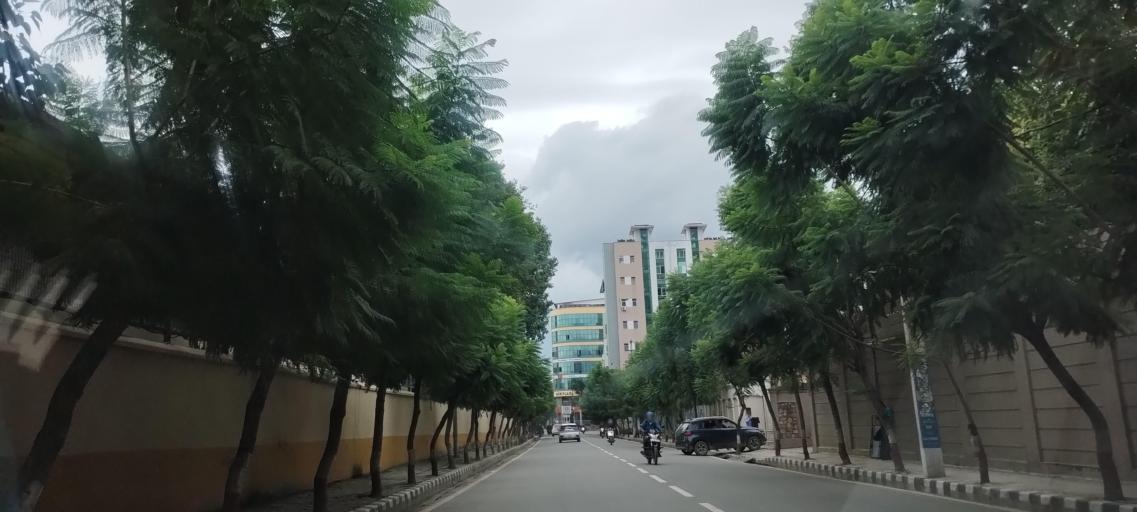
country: NP
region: Central Region
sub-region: Bagmati Zone
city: Kathmandu
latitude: 27.7165
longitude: 85.3275
